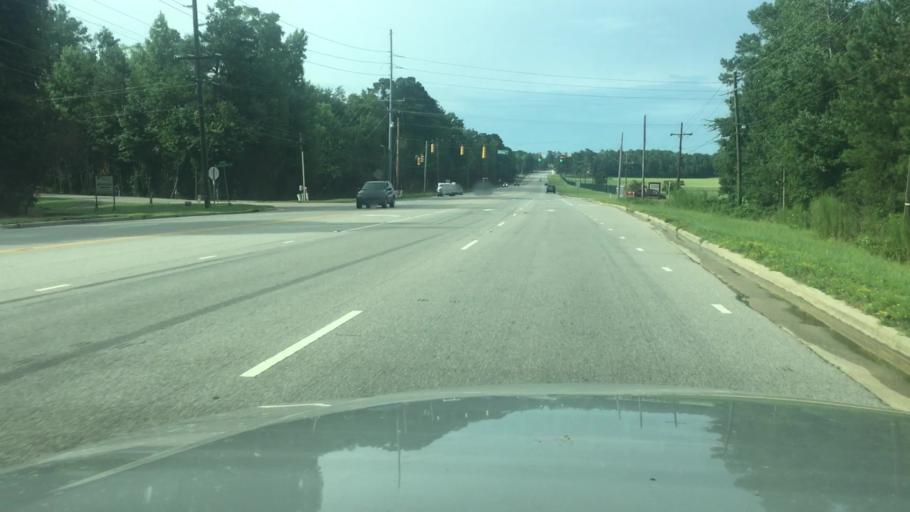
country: US
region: North Carolina
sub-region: Cumberland County
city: Eastover
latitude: 35.1670
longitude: -78.8630
